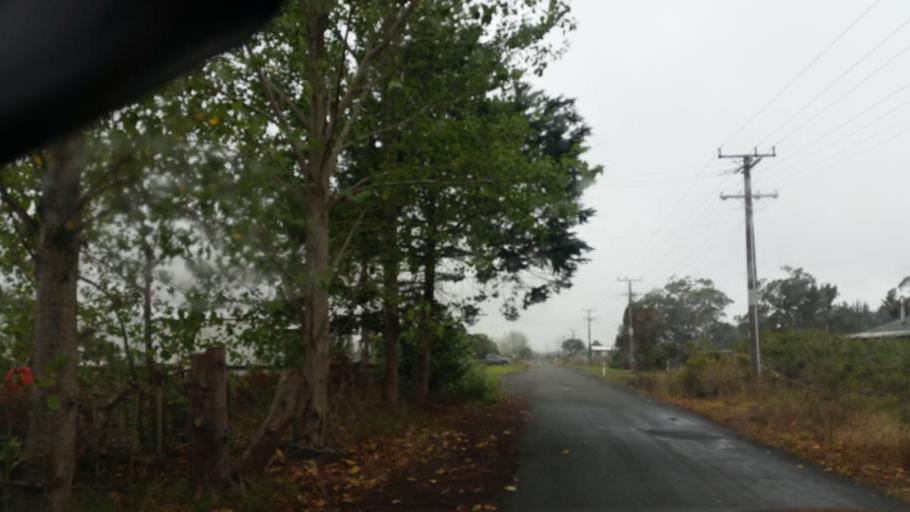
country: NZ
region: Northland
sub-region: Kaipara District
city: Dargaville
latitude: -35.8326
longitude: 173.7507
